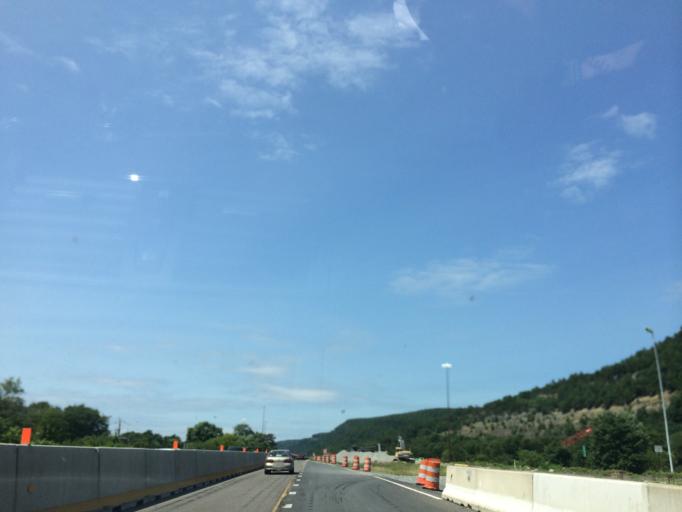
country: US
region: Pennsylvania
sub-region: Pike County
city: Matamoras
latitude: 41.3580
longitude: -74.7112
